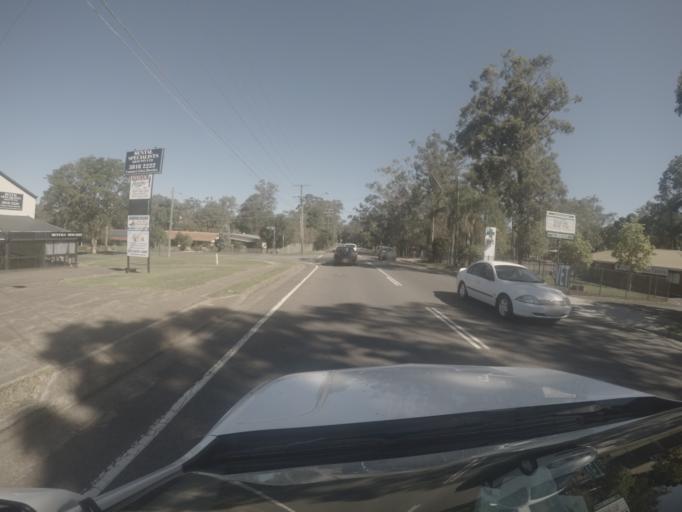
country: AU
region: Queensland
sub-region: Ipswich
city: Springfield
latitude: -27.6304
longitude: 152.9160
